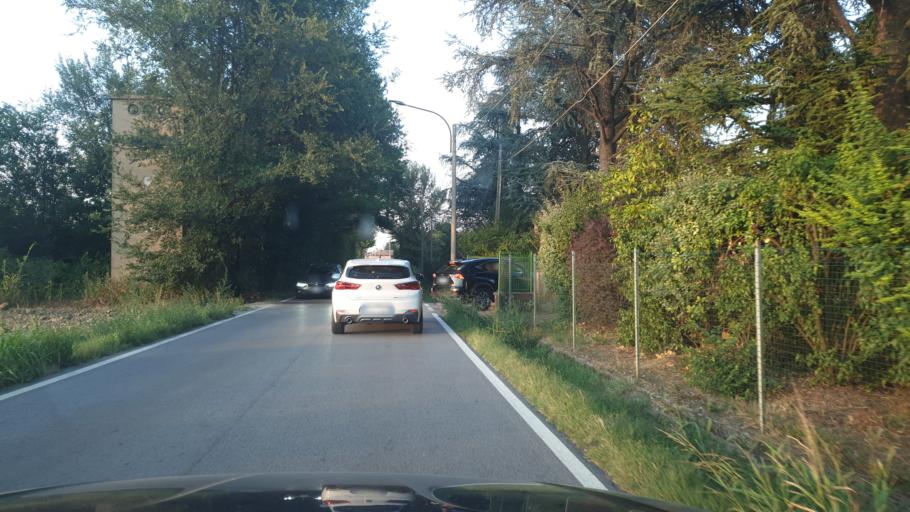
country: IT
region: Emilia-Romagna
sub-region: Provincia di Bologna
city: Quarto Inferiore
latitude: 44.5360
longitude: 11.3910
